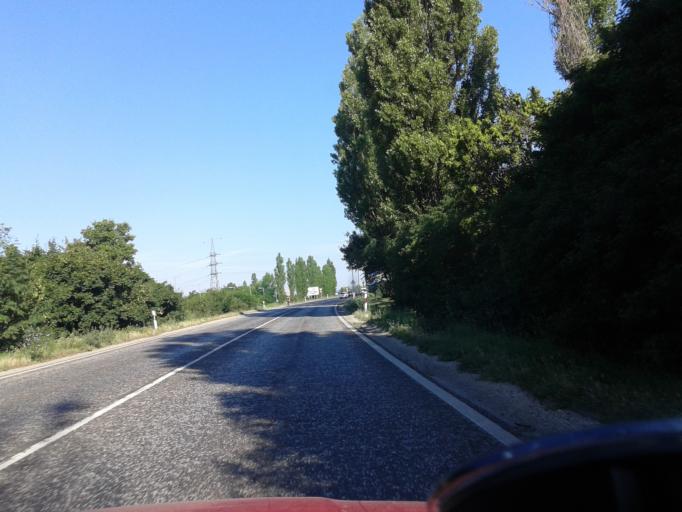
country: HU
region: Pest
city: Biatorbagy
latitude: 47.4737
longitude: 18.8468
